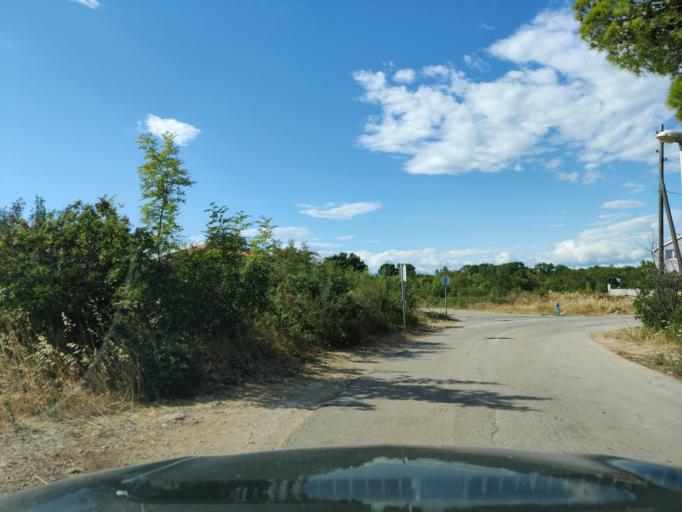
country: HR
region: Sibensko-Kniniska
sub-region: Grad Sibenik
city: Sibenik
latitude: 43.7273
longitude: 15.8464
